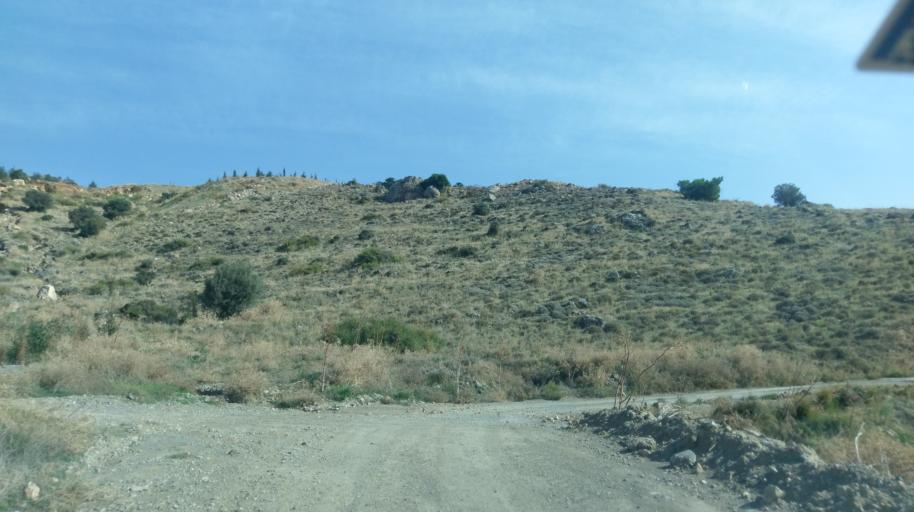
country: CY
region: Lefkosia
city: Nicosia
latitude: 35.2643
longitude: 33.4083
